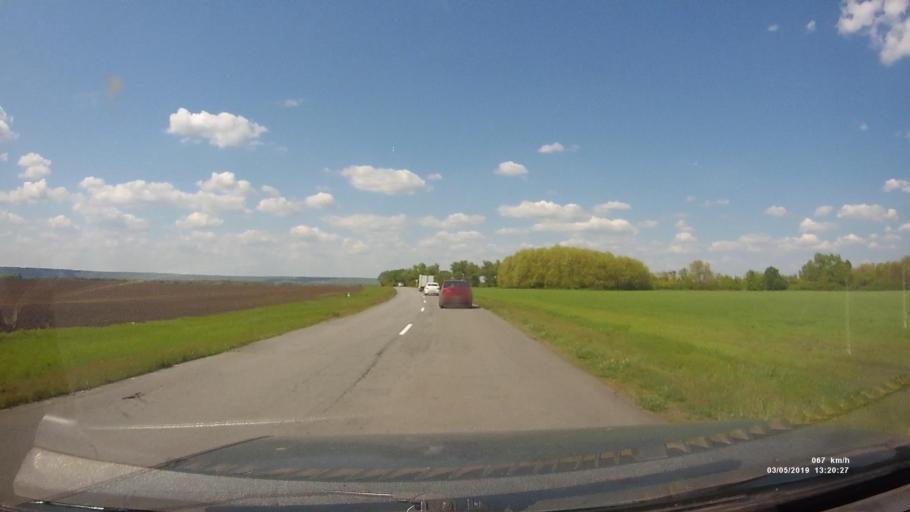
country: RU
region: Rostov
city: Semikarakorsk
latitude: 47.5463
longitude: 40.7535
